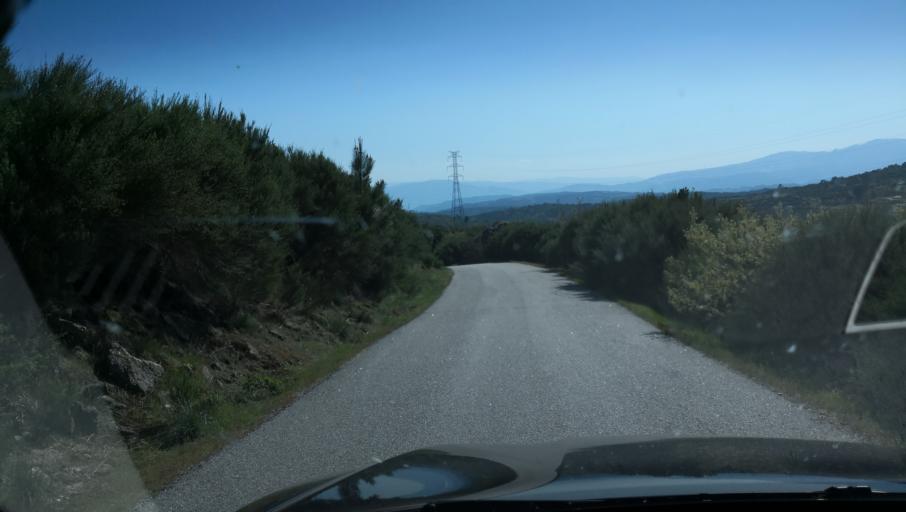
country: PT
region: Vila Real
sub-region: Sabrosa
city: Sabrosa
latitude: 41.2953
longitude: -7.6362
